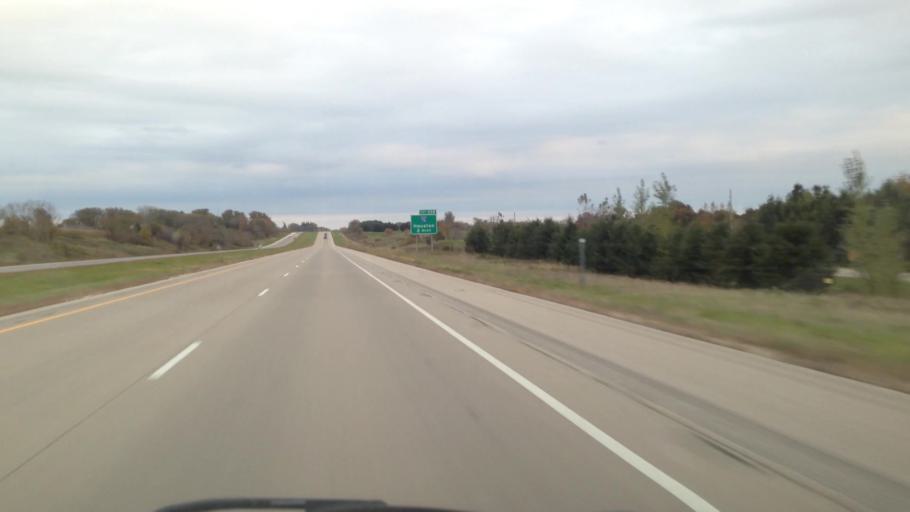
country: US
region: Minnesota
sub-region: Winona County
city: Winona
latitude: 43.9379
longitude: -91.6290
